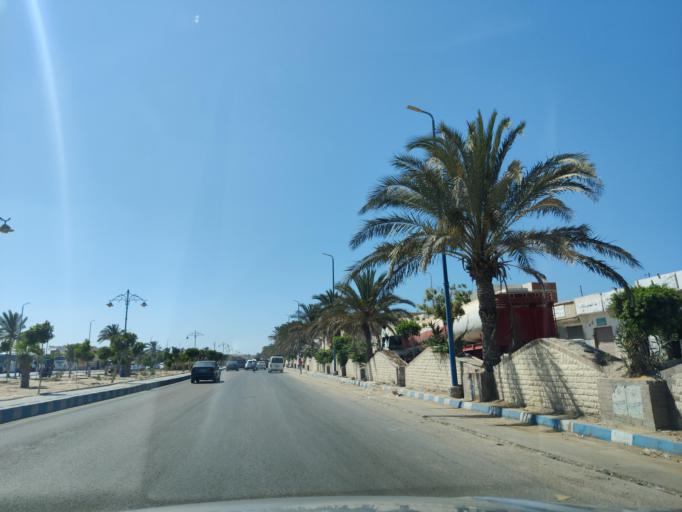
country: EG
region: Muhafazat Matruh
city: Mersa Matruh
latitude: 31.3377
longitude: 27.2526
